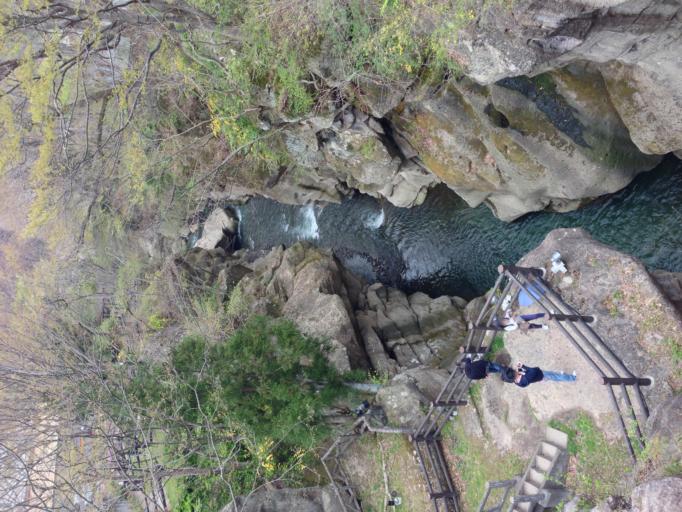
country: JP
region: Miyagi
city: Sendai
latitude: 38.2245
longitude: 140.7288
